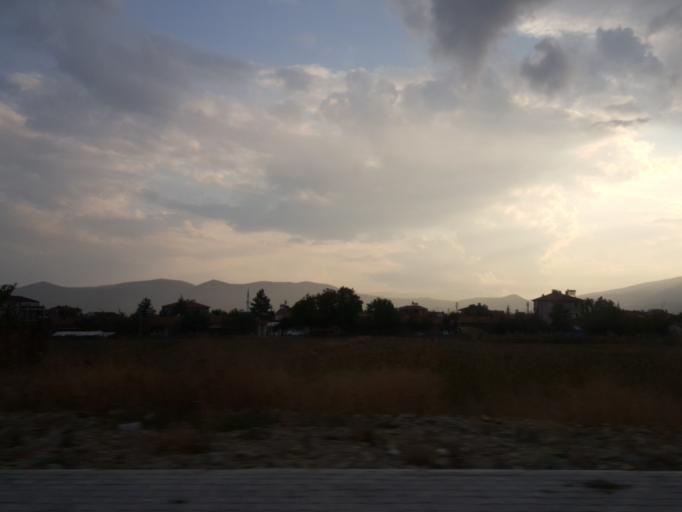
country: TR
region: Amasya
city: Gumushacikoy
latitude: 40.8794
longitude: 35.2251
